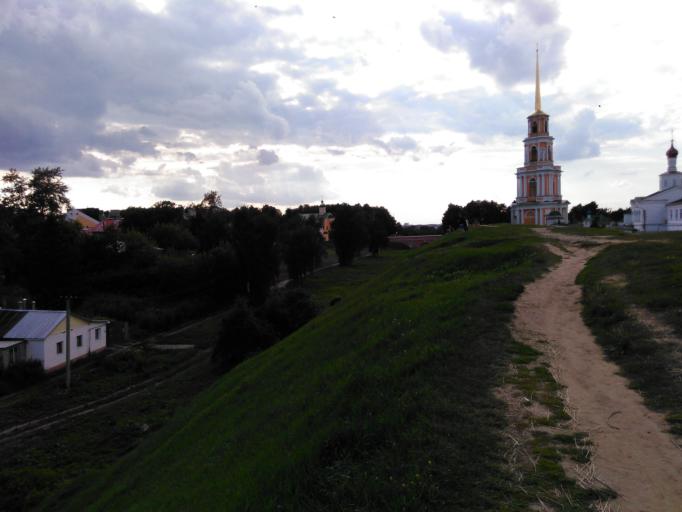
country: RU
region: Rjazan
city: Ryazan'
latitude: 54.6346
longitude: 39.7517
